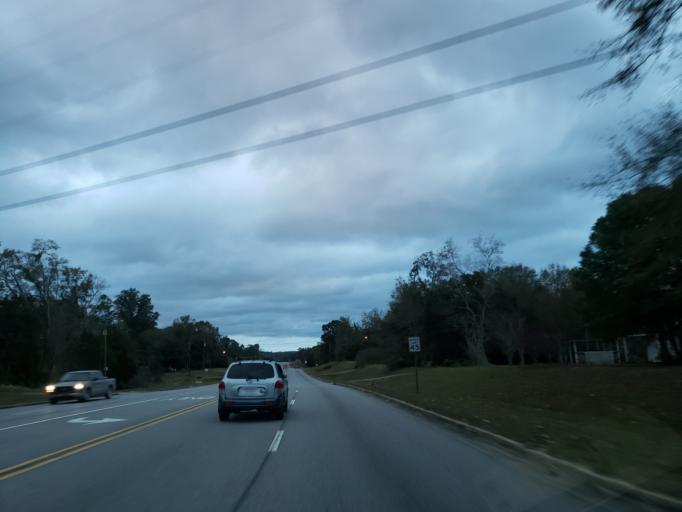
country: US
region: Alabama
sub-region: Mobile County
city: Chickasaw
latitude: 30.7942
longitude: -88.2255
